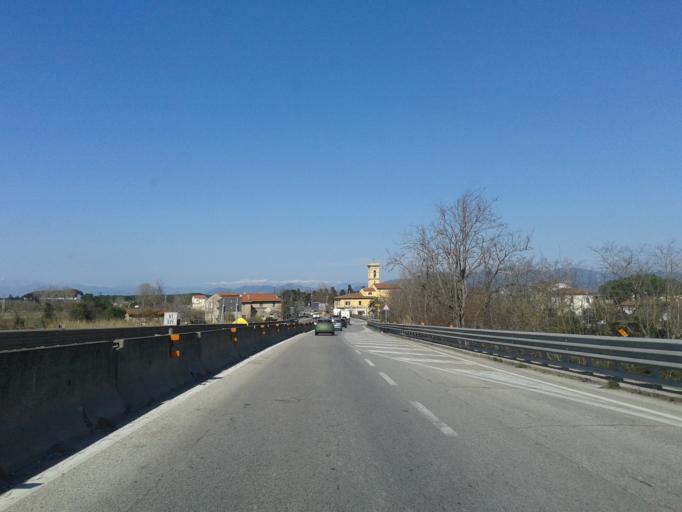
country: IT
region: Tuscany
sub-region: Provincia di Livorno
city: Livorno
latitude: 43.5968
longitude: 10.3506
